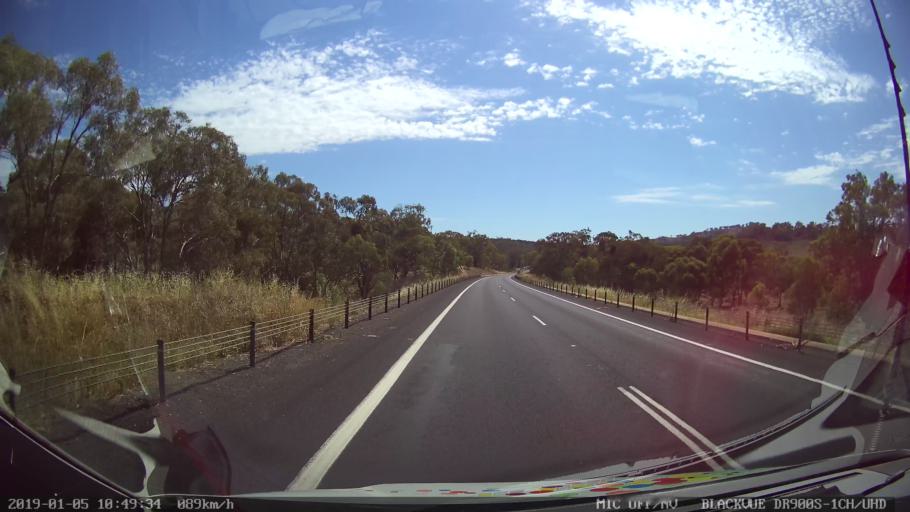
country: AU
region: New South Wales
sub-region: Warrumbungle Shire
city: Coonabarabran
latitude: -31.4332
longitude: 149.0628
